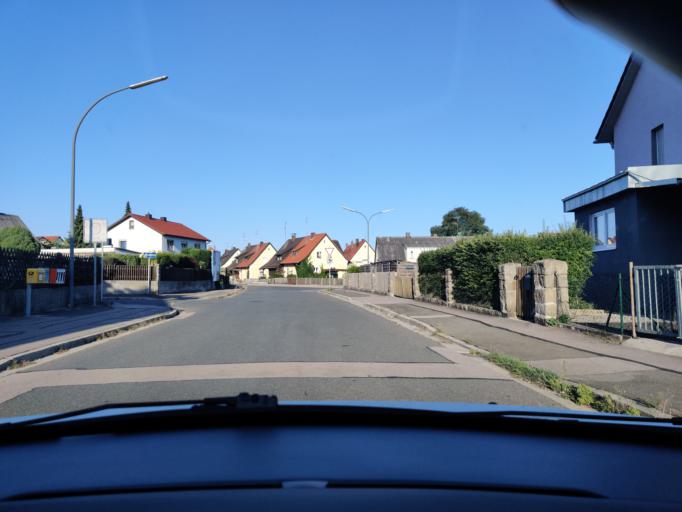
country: DE
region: Bavaria
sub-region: Upper Palatinate
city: Schwarzenfeld
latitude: 49.3870
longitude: 12.1307
